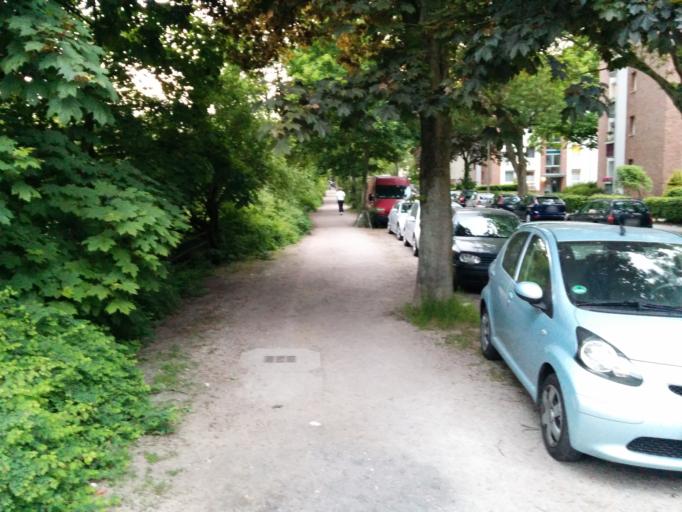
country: DE
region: Hamburg
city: Borgfelde
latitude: 53.5722
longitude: 10.0440
